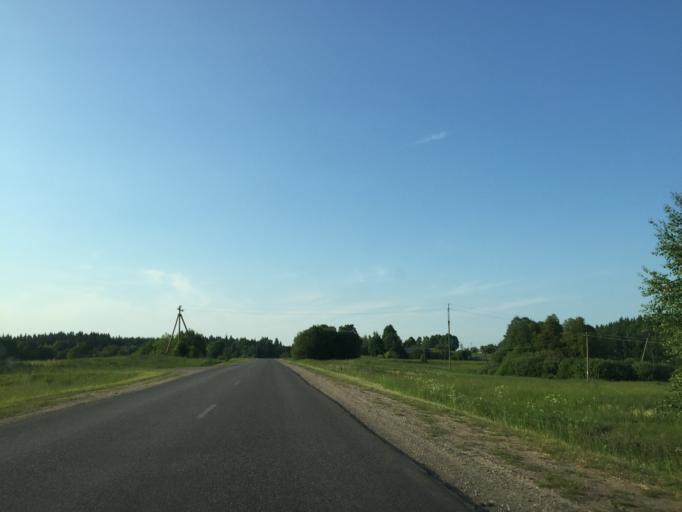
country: LT
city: Plateliai
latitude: 56.0563
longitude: 21.8196
